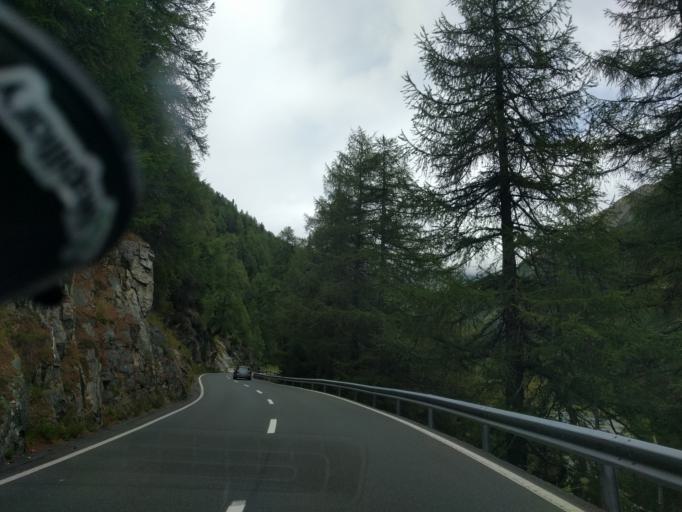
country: CH
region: Grisons
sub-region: Inn District
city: Zernez
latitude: 46.7546
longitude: 10.0307
